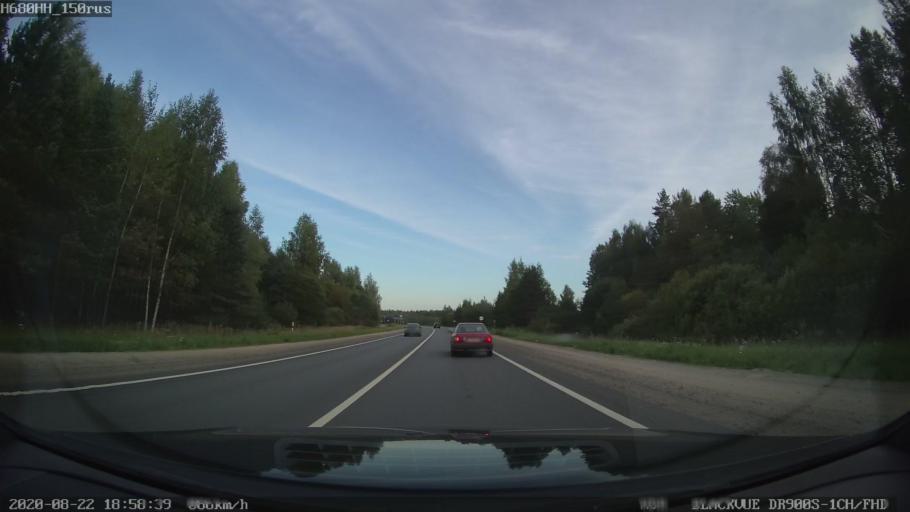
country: RU
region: Tverskaya
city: Rameshki
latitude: 57.1510
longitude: 36.0794
